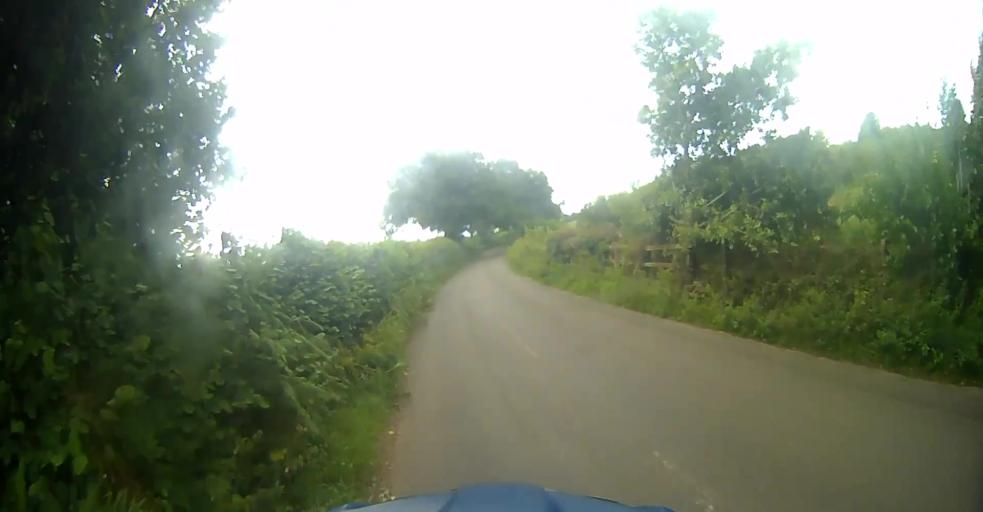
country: GB
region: England
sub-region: Hampshire
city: Alton
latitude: 51.1849
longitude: -1.0194
